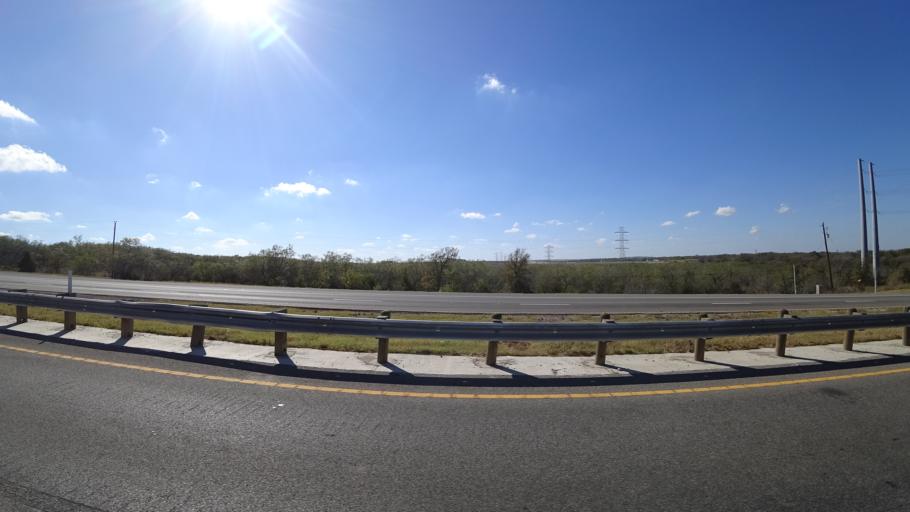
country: US
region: Texas
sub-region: Travis County
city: Garfield
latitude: 30.1881
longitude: -97.6172
